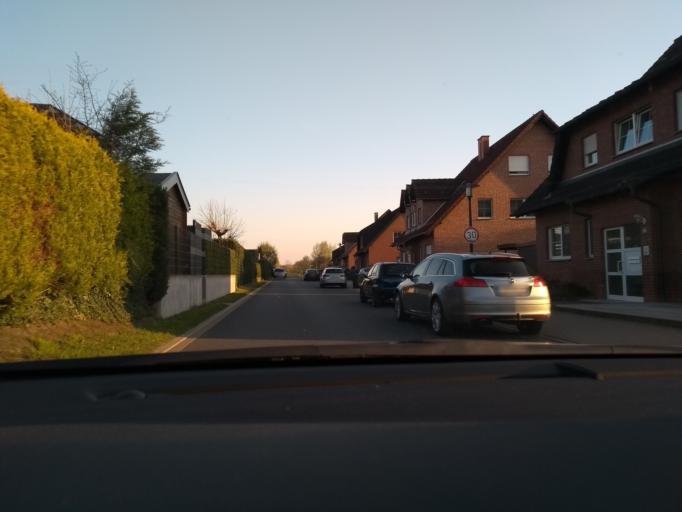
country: DE
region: North Rhine-Westphalia
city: Selm
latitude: 51.6919
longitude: 7.4556
